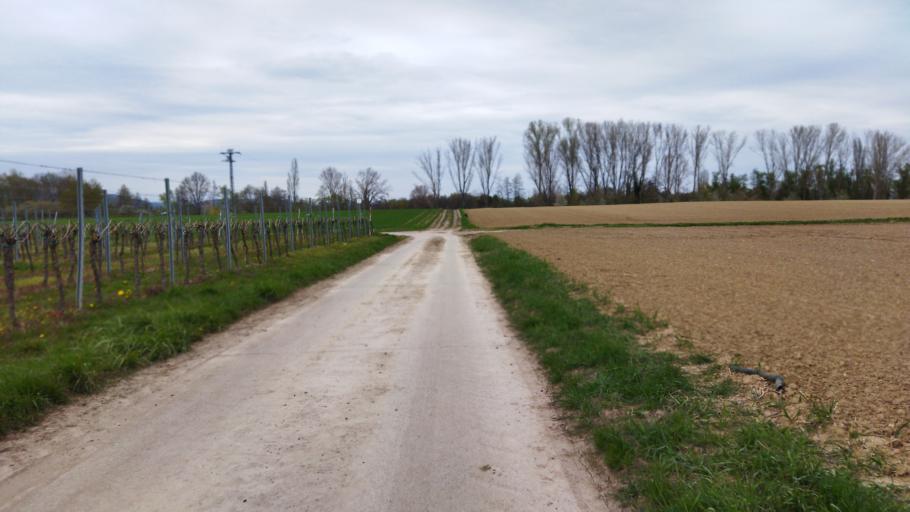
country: DE
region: Rheinland-Pfalz
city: Kleinfischlingen
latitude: 49.2702
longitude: 8.1883
